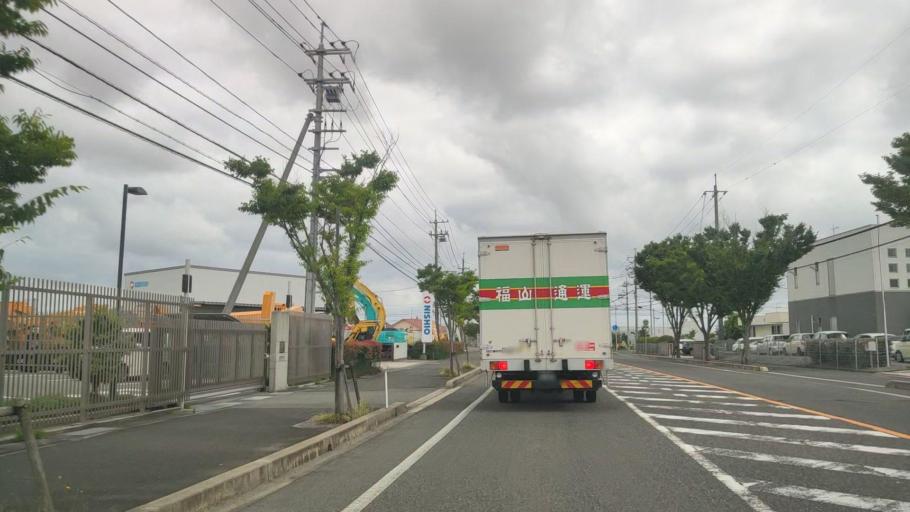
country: JP
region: Tottori
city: Yonago
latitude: 35.4305
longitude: 133.3936
